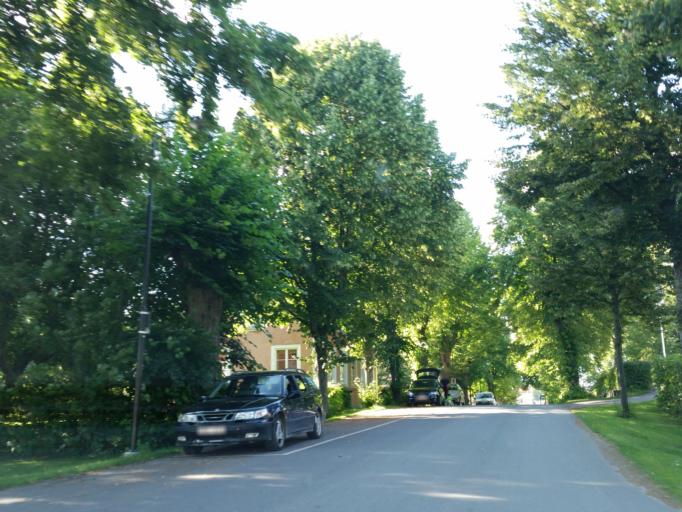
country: SE
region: Soedermanland
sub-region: Trosa Kommun
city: Trosa
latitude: 58.8936
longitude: 17.5493
